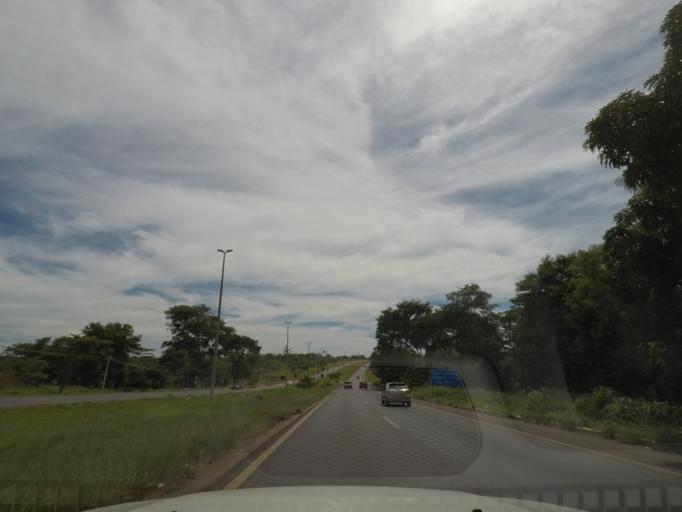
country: BR
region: Goias
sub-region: Planaltina
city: Planaltina
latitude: -15.5958
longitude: -47.6701
